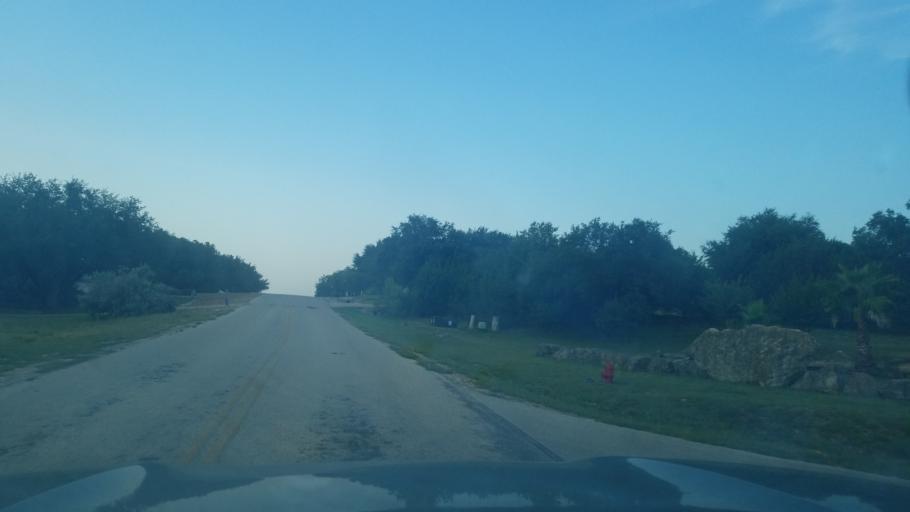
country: US
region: Texas
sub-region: Comal County
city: Bulverde
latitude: 29.8236
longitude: -98.4030
